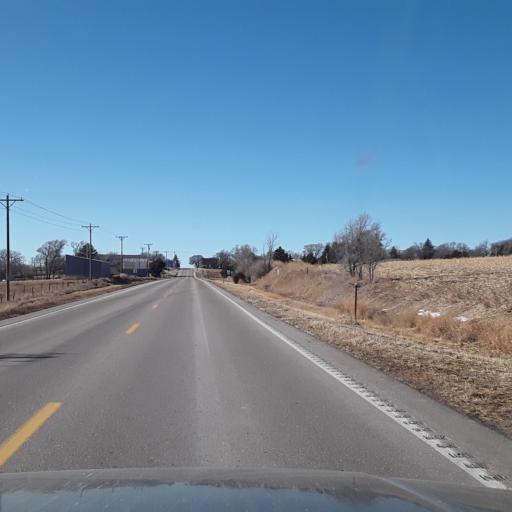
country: US
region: Nebraska
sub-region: Dawson County
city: Gothenburg
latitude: 40.7057
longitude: -100.2079
